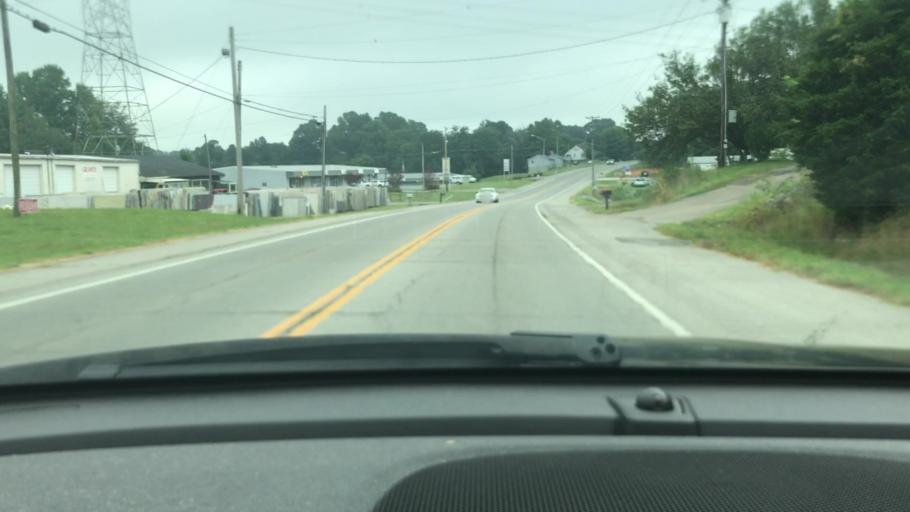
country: US
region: Tennessee
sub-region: Sumner County
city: Millersville
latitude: 36.4239
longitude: -86.6943
